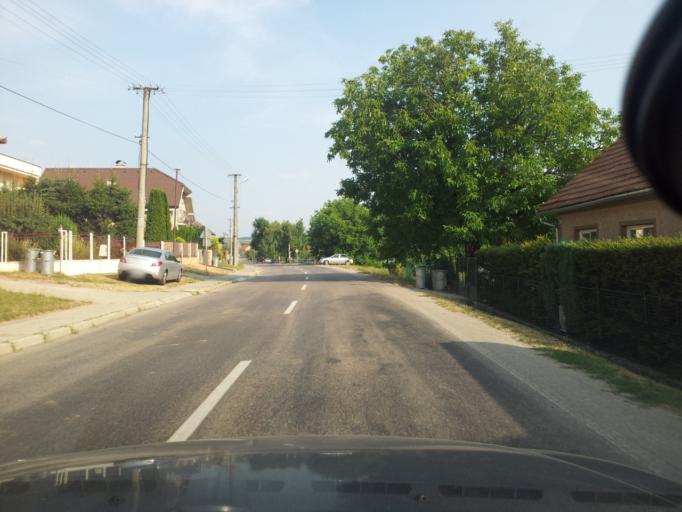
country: SK
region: Nitriansky
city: Trencianske Teplice
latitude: 48.8075
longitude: 18.1883
